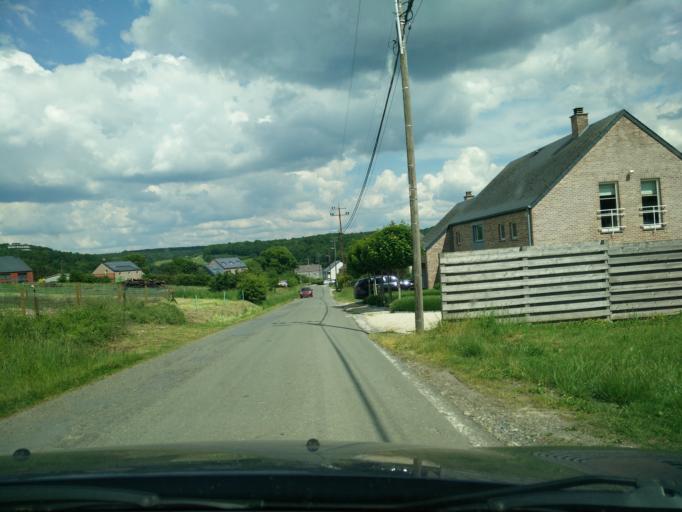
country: BE
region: Wallonia
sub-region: Province de Namur
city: Couvin
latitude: 50.0897
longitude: 4.5851
